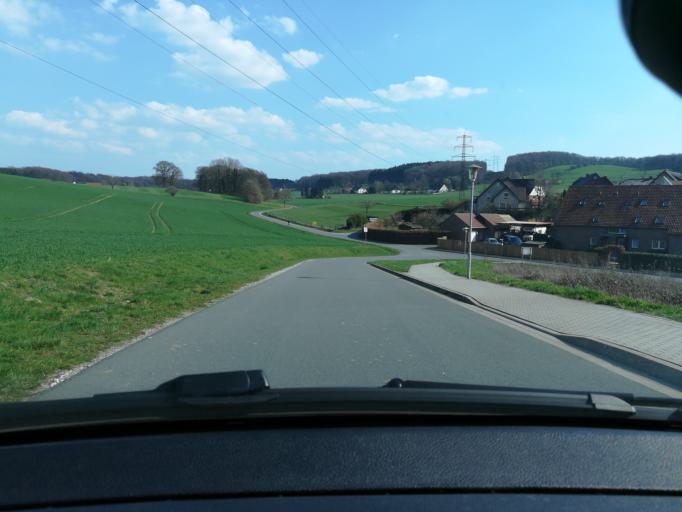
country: DE
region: North Rhine-Westphalia
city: Borgholzhausen
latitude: 52.1022
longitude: 8.3155
